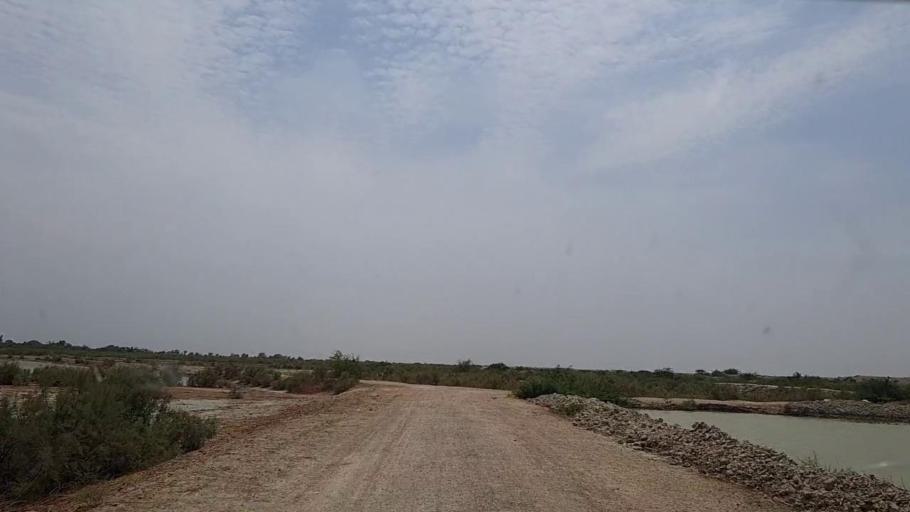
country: PK
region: Sindh
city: Phulji
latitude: 26.8743
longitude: 67.6524
